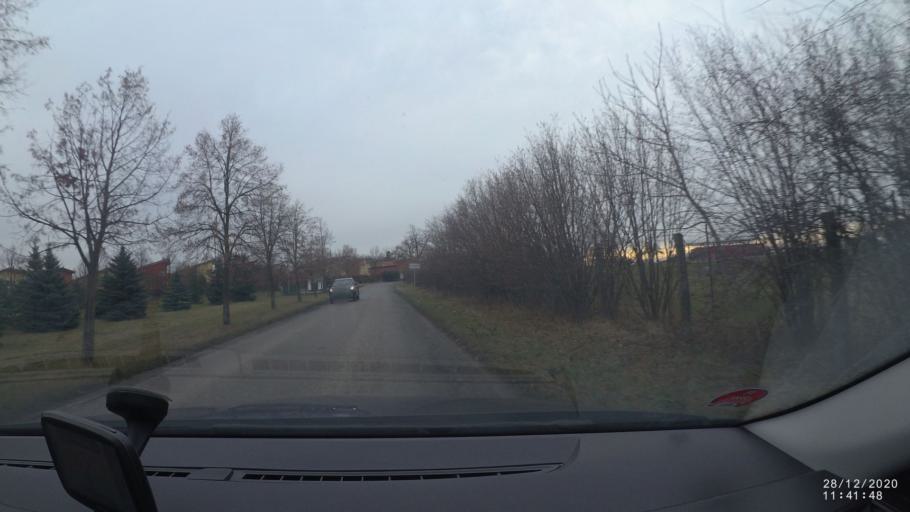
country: CZ
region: Central Bohemia
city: Zelenec
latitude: 50.1390
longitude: 14.6588
